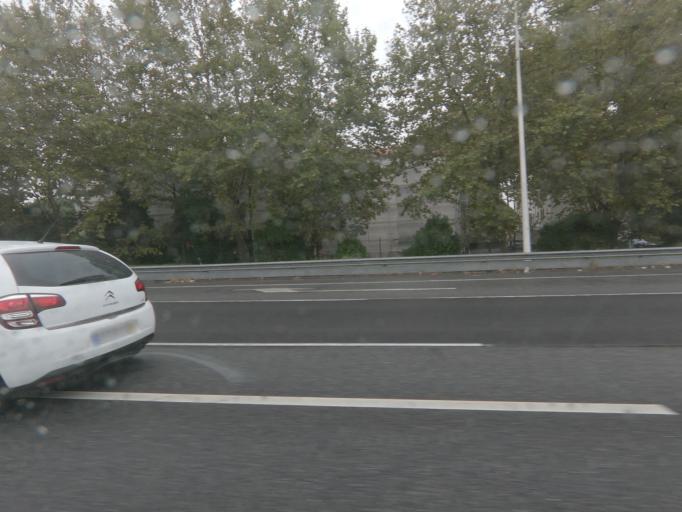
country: PT
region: Porto
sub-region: Porto
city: Porto
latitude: 41.1739
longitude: -8.6184
